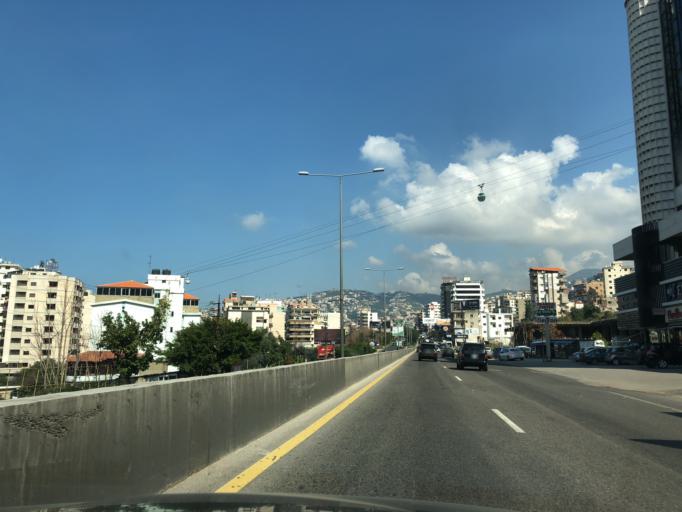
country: LB
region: Mont-Liban
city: Djounie
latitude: 33.9900
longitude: 35.6425
